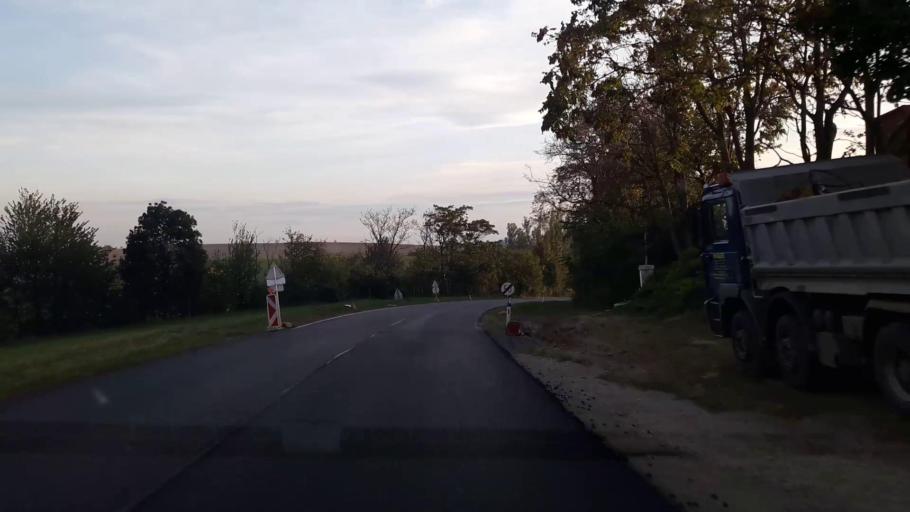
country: AT
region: Lower Austria
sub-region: Politischer Bezirk Korneuburg
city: Grossrussbach
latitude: 48.4646
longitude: 16.3778
